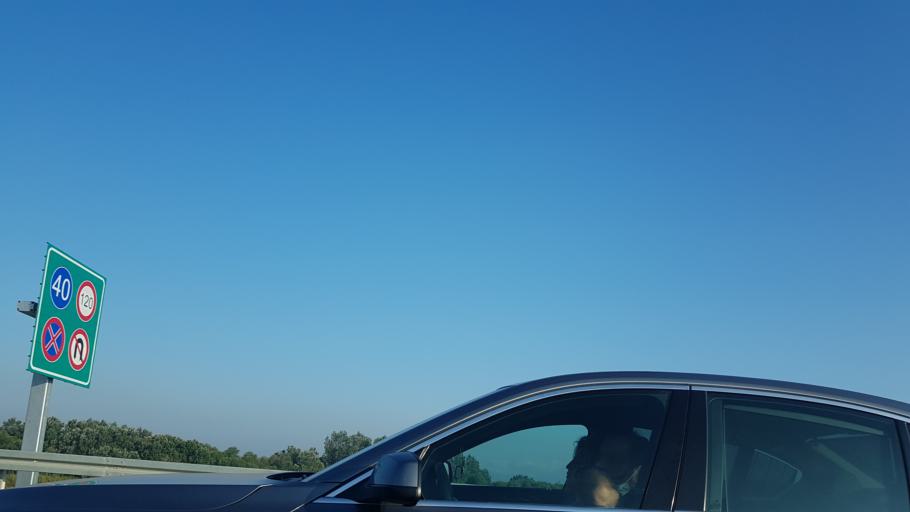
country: TR
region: Bursa
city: Karacabey
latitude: 40.1866
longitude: 28.3362
